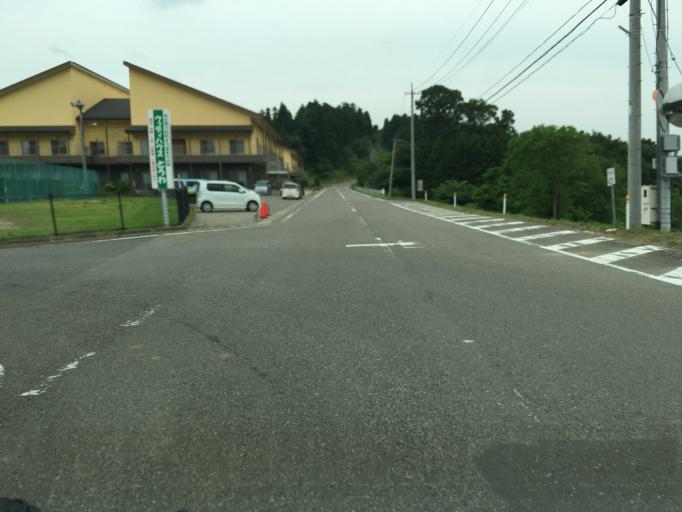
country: JP
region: Fukushima
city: Nihommatsu
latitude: 37.6302
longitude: 140.5259
